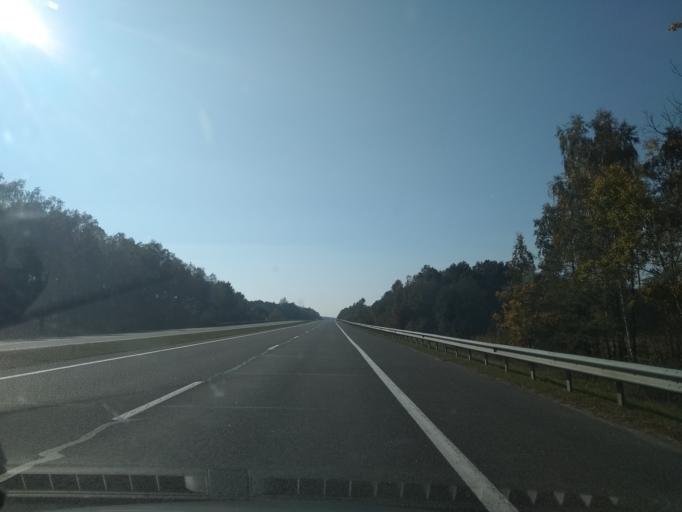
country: BY
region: Brest
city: Horad Kobryn
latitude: 52.2826
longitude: 24.5578
